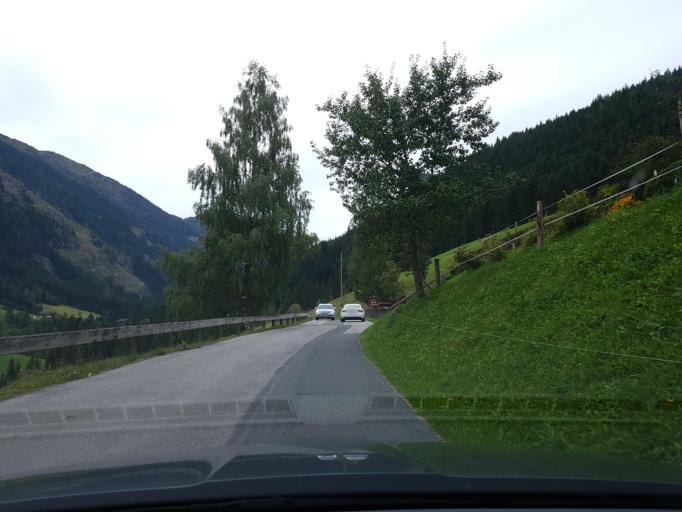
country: AT
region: Salzburg
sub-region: Politischer Bezirk Sankt Johann im Pongau
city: Forstau
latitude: 47.3624
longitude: 13.5606
